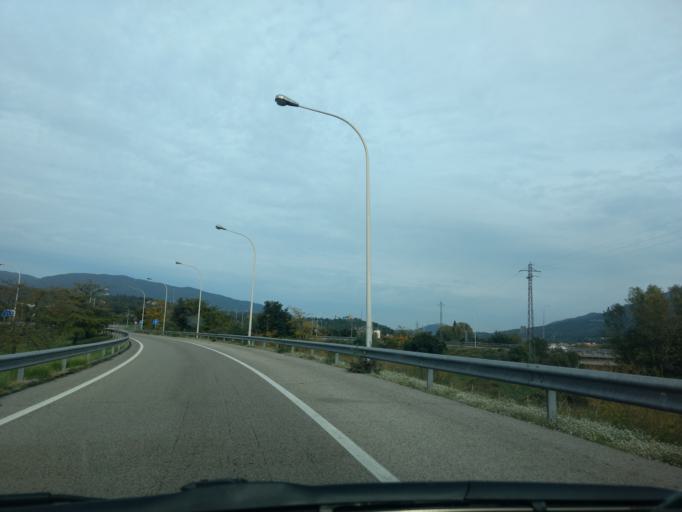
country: ES
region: Catalonia
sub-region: Provincia de Girona
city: la Jonquera
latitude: 42.4069
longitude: 2.8747
